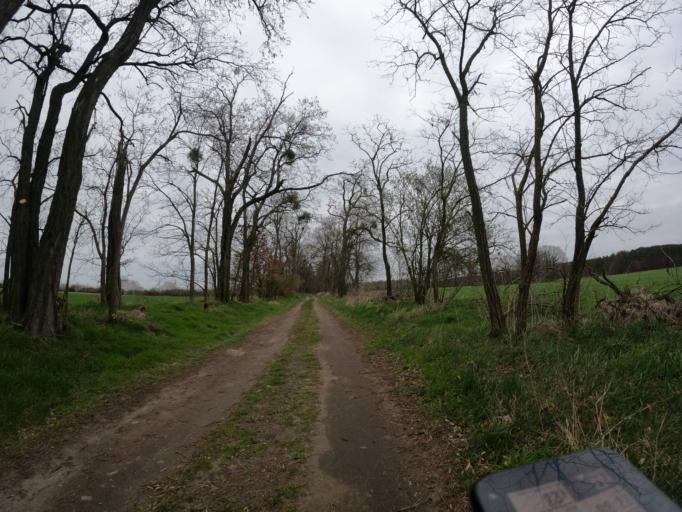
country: DE
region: Brandenburg
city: Werftpfuhl
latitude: 52.5943
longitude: 13.8048
